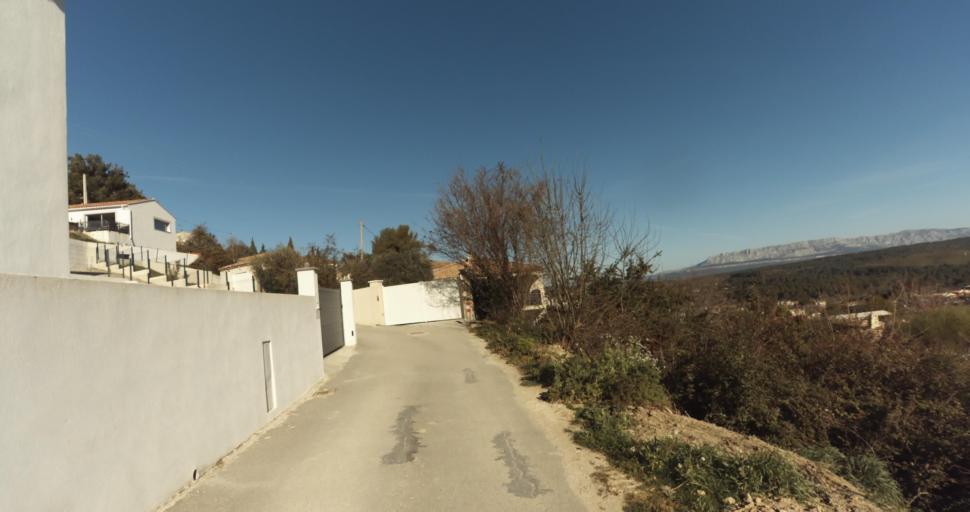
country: FR
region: Provence-Alpes-Cote d'Azur
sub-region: Departement des Bouches-du-Rhone
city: Cadolive
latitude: 43.3898
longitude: 5.5483
